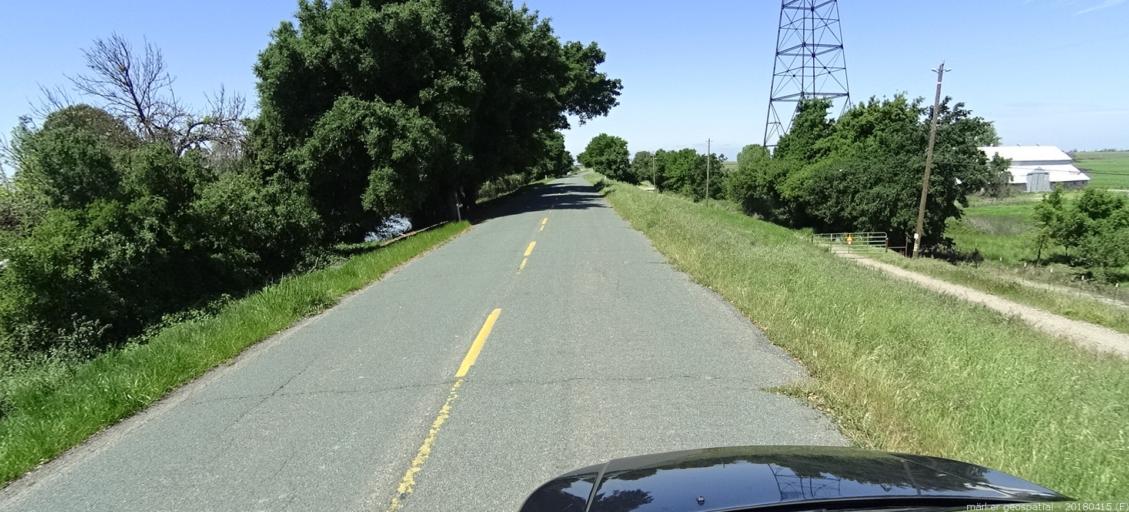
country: US
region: California
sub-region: Solano County
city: Rio Vista
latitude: 38.1686
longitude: -121.6271
